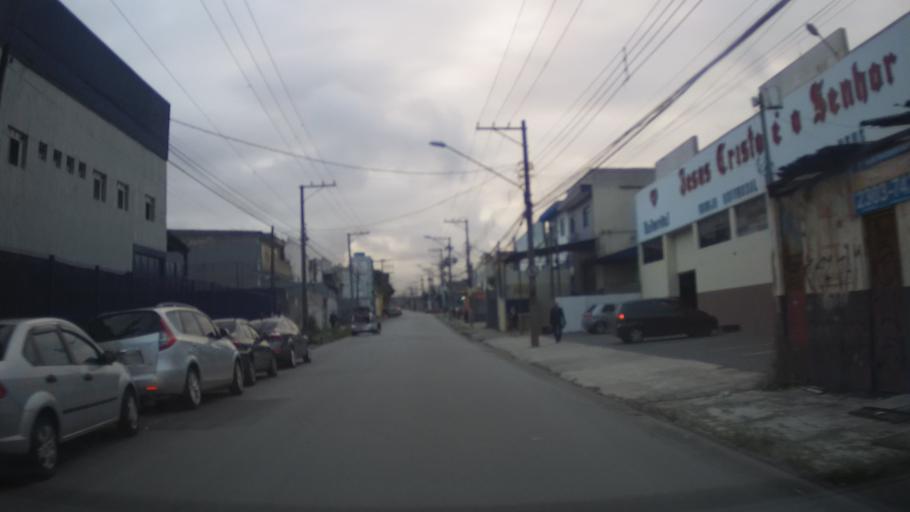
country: BR
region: Sao Paulo
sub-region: Guarulhos
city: Guarulhos
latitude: -23.4588
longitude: -46.4644
